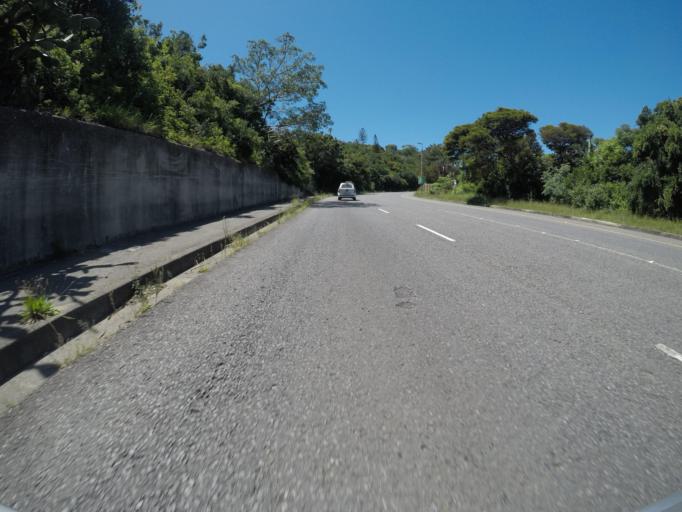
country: ZA
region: Eastern Cape
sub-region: Buffalo City Metropolitan Municipality
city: East London
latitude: -32.9714
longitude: 27.9286
